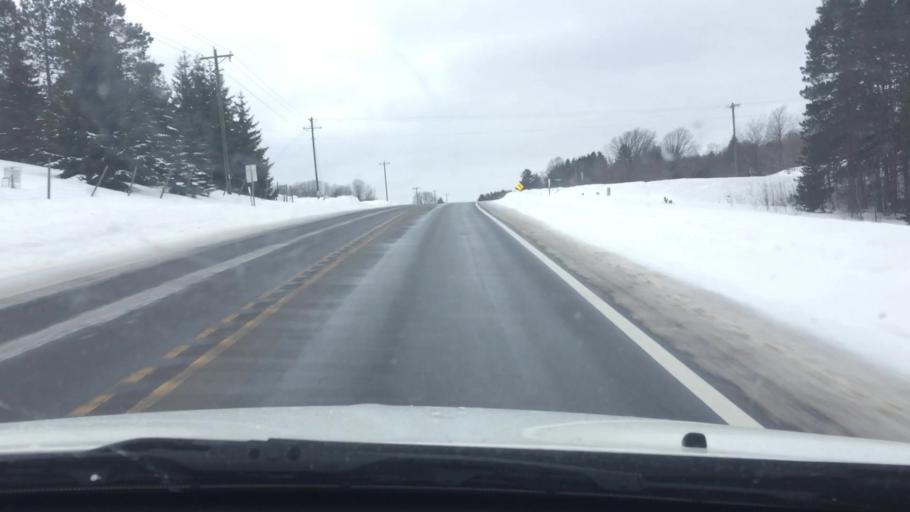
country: US
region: Michigan
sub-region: Charlevoix County
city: Boyne City
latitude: 45.0951
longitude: -84.9779
